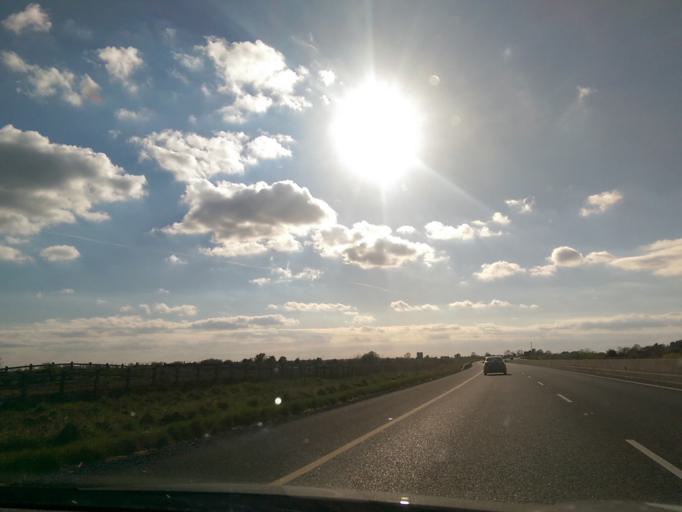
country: IE
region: Connaught
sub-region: County Galway
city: Athenry
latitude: 53.2698
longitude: -8.6564
